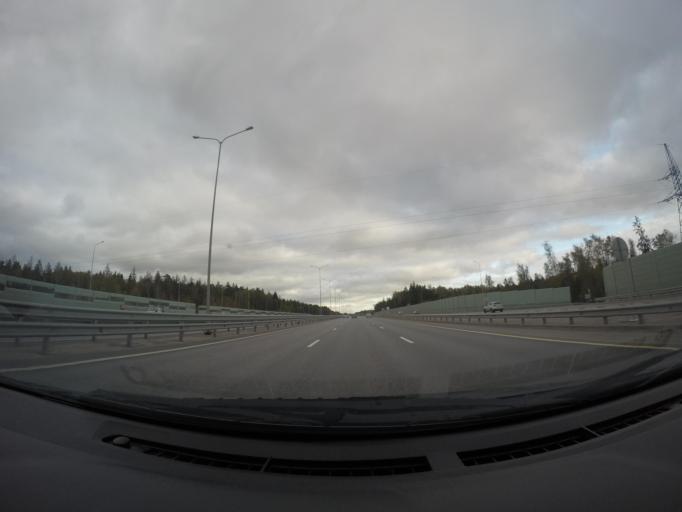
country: RU
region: Moskovskaya
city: Golitsyno
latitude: 55.5982
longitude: 36.9637
